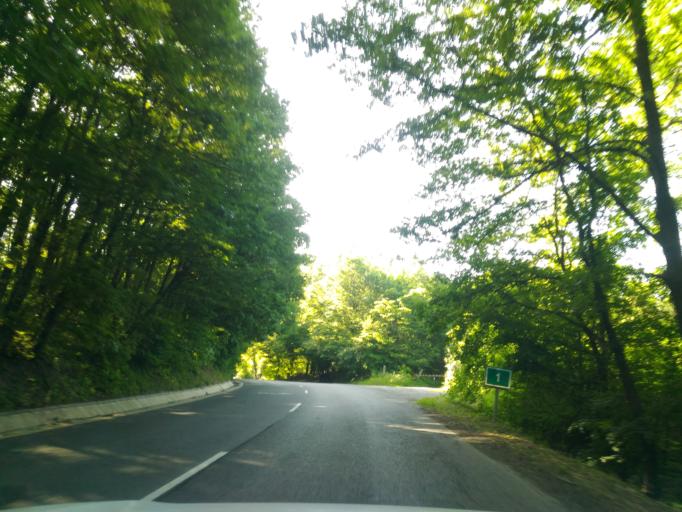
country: HU
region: Baranya
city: Komlo
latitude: 46.1859
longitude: 18.3064
